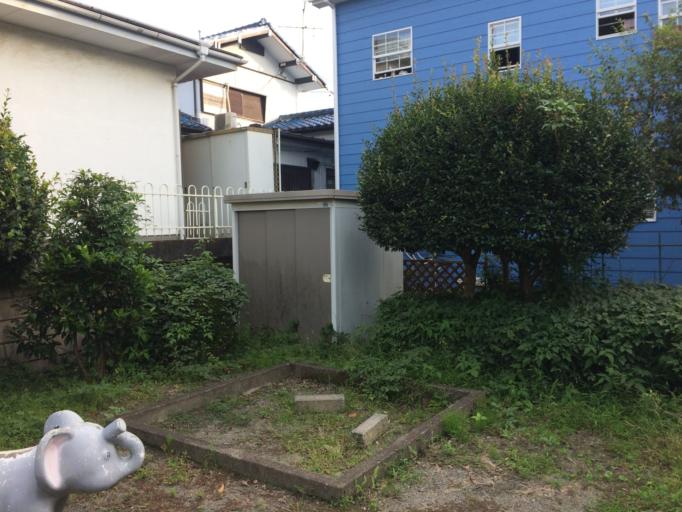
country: JP
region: Shizuoka
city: Shizuoka-shi
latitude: 35.0032
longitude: 138.4542
